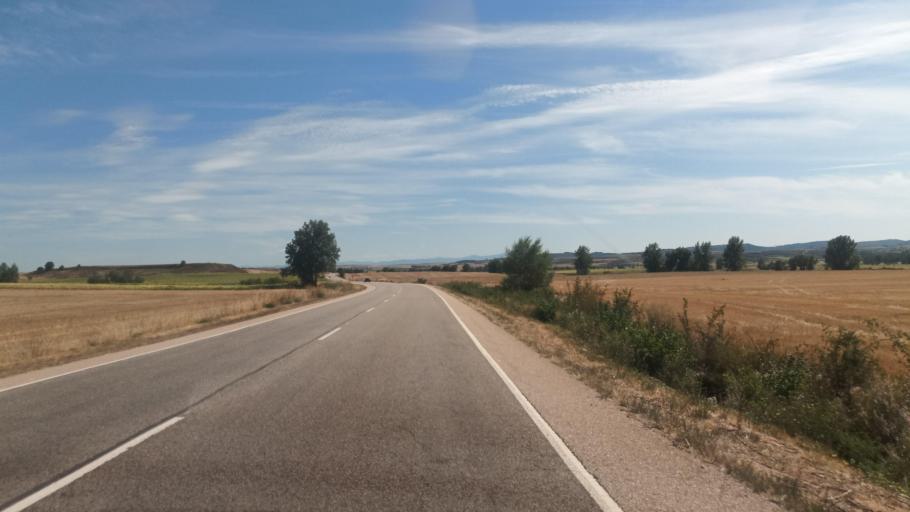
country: ES
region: Castille and Leon
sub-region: Provincia de Burgos
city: Quintanabureba
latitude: 42.6137
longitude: -3.3574
